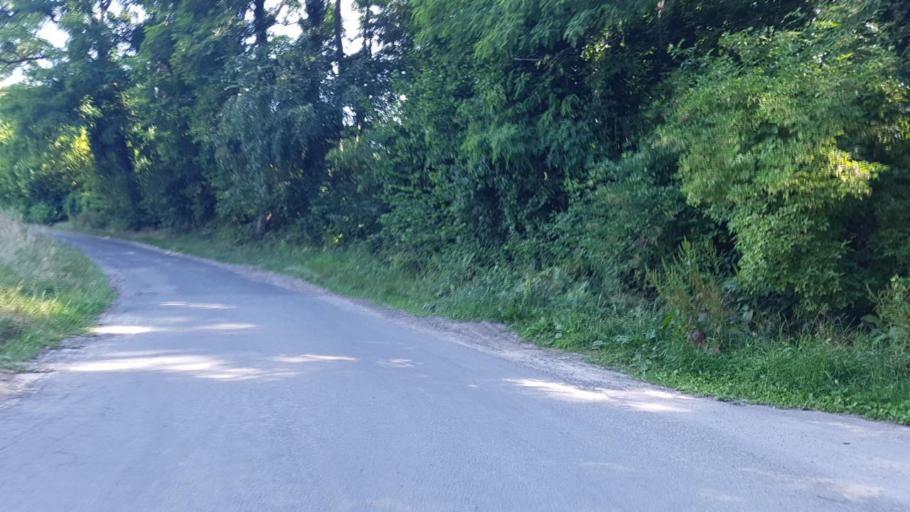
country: FR
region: Picardie
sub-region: Departement de l'Oise
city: Pontpoint
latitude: 49.2907
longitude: 2.6469
